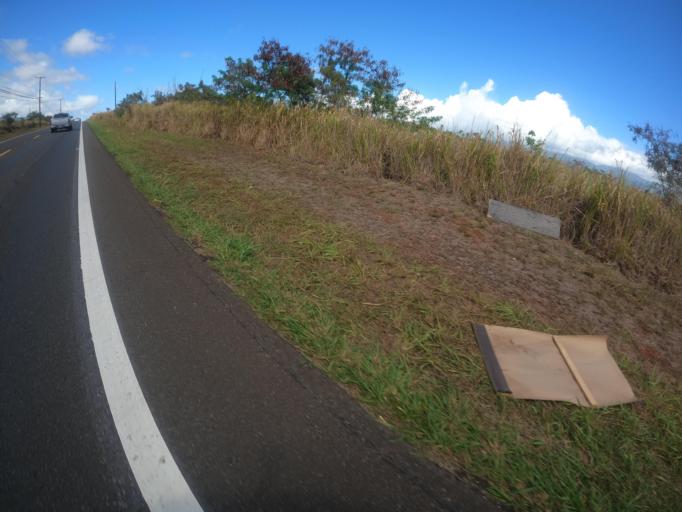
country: US
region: Hawaii
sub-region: Honolulu County
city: Village Park
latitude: 21.4083
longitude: -158.0433
